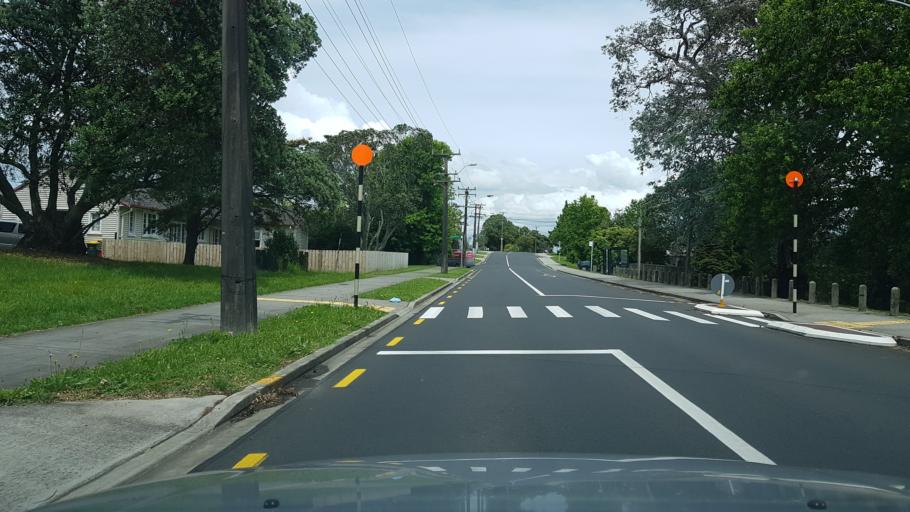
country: NZ
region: Auckland
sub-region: Auckland
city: North Shore
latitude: -36.7977
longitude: 174.7523
